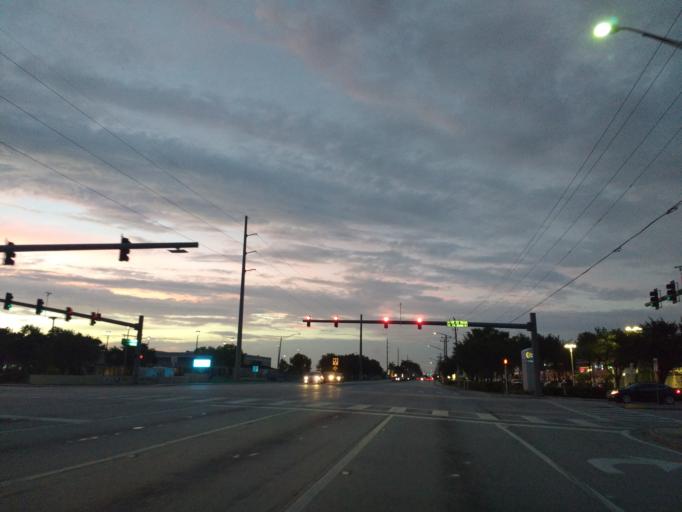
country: US
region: Florida
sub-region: Lee County
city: Cape Coral
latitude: 26.6073
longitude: -81.9742
